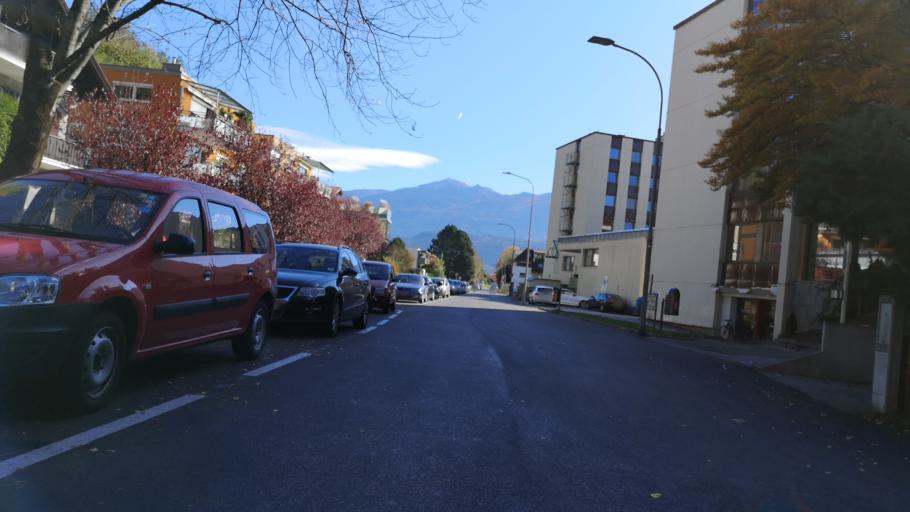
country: AT
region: Tyrol
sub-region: Politischer Bezirk Innsbruck Land
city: Vols
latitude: 47.2657
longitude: 11.3587
